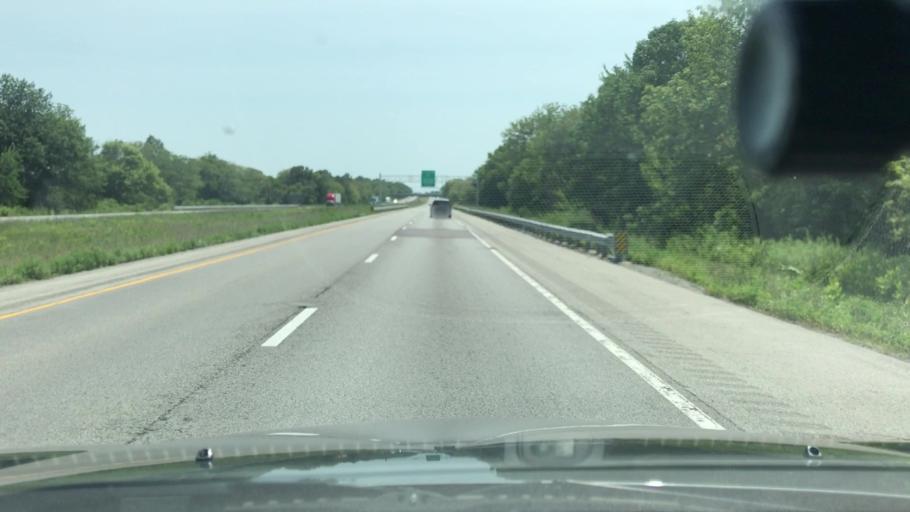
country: US
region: Illinois
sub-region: Jefferson County
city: Mount Vernon
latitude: 38.3463
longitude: -88.9782
